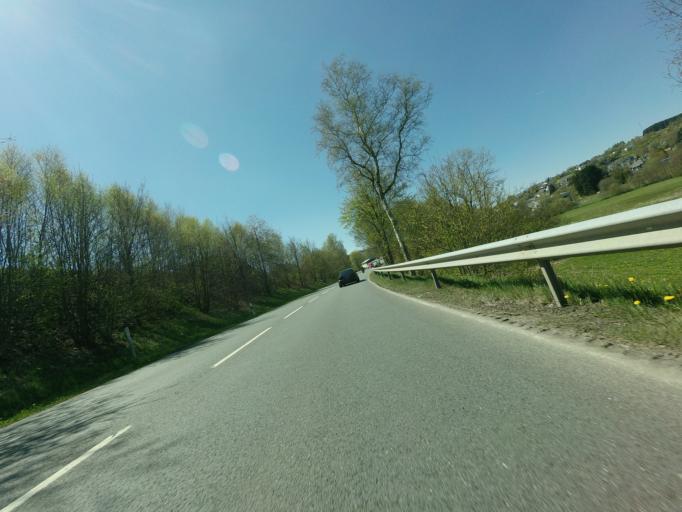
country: DE
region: North Rhine-Westphalia
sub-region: Regierungsbezirk Arnsberg
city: Erndtebruck
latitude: 50.9946
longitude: 8.2625
